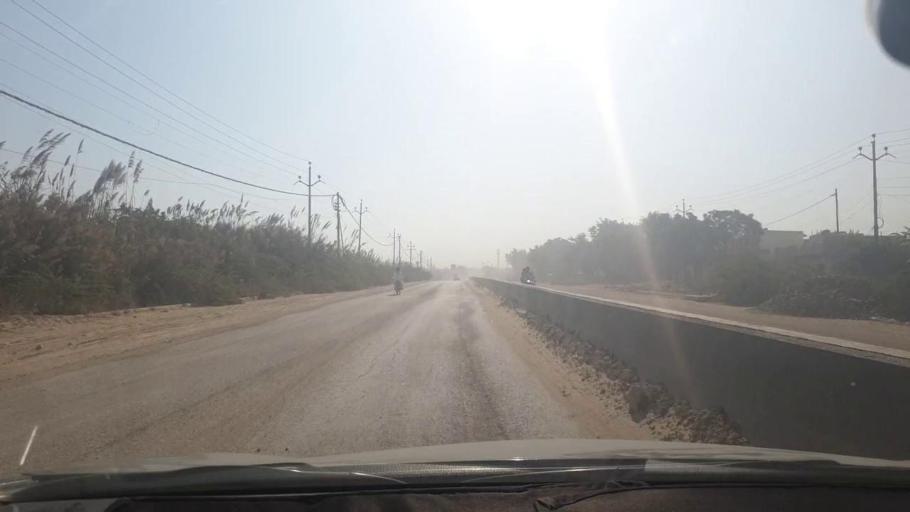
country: PK
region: Sindh
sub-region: Karachi District
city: Karachi
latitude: 25.0046
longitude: 67.0329
